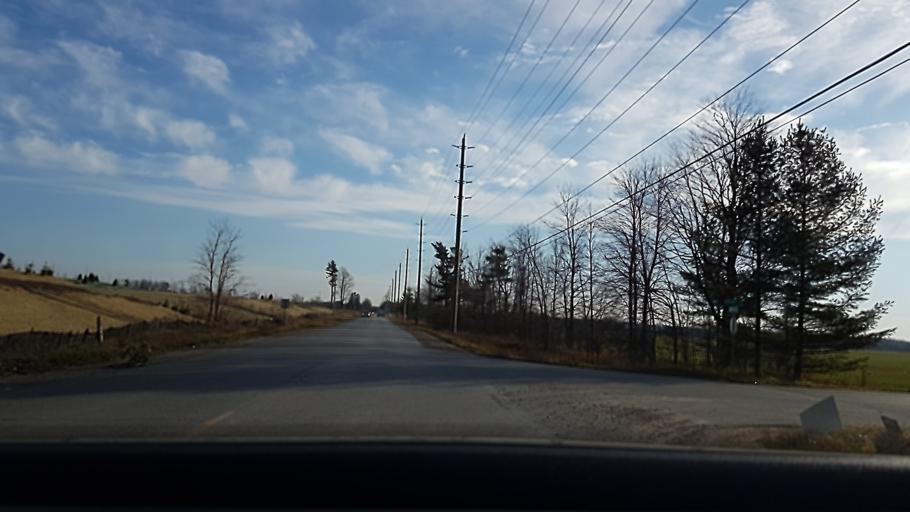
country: CA
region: Ontario
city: Barrie
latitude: 44.3844
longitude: -79.5553
